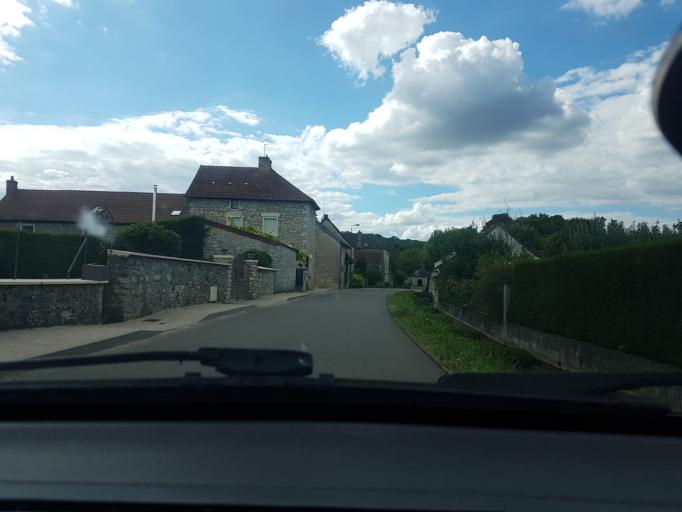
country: FR
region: Bourgogne
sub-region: Departement de Saone-et-Loire
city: Fontaines
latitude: 46.8487
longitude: 4.7620
